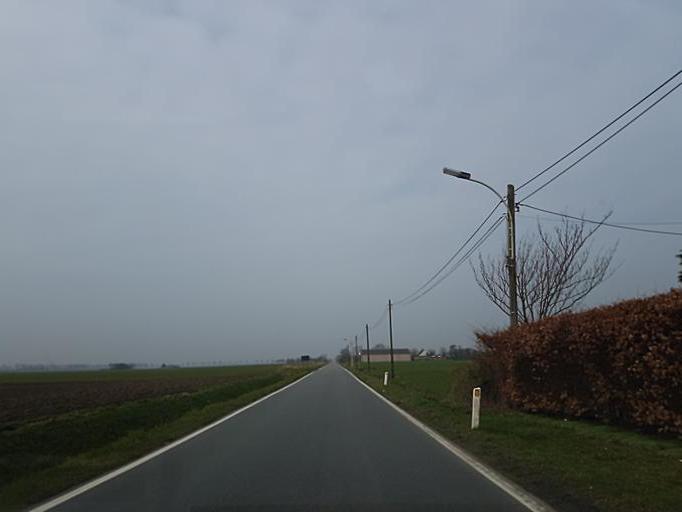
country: BE
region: Flanders
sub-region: Provincie Oost-Vlaanderen
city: Beveren
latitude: 51.3018
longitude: 4.2331
